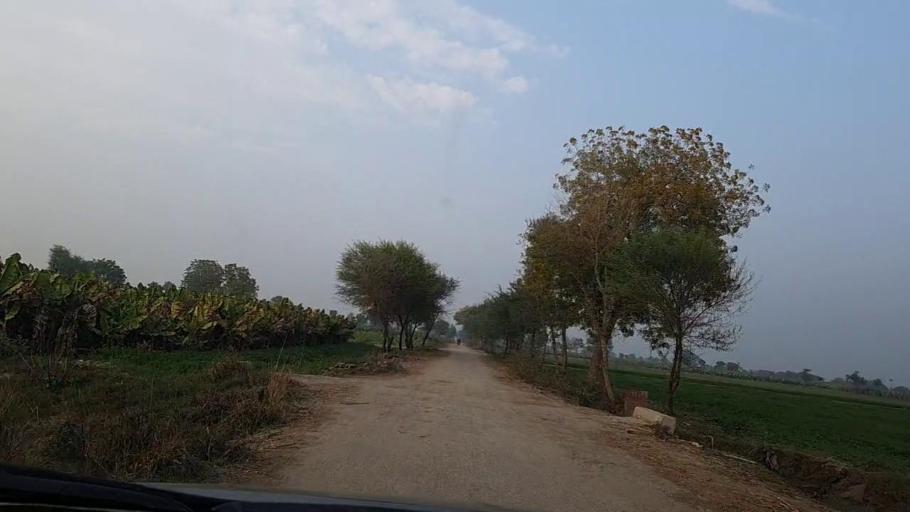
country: PK
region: Sindh
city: Nawabshah
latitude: 26.2861
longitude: 68.3211
